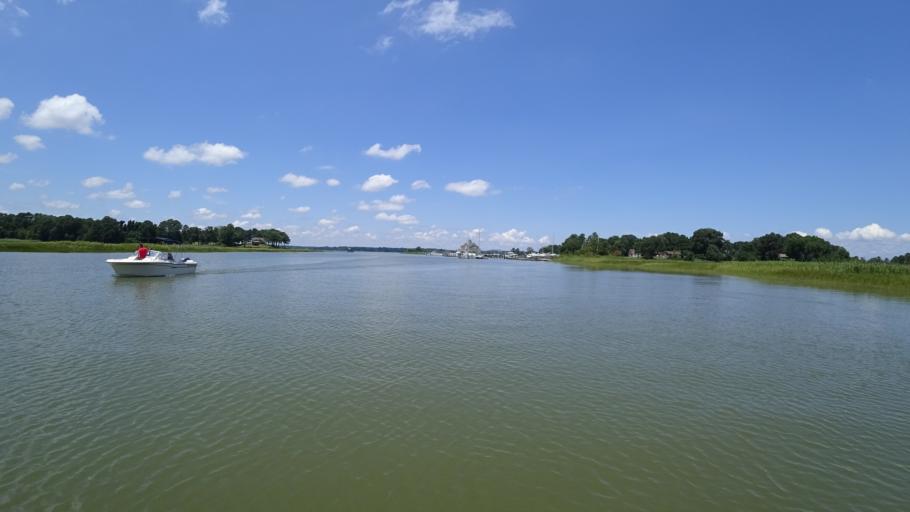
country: US
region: Virginia
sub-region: Isle of Wight County
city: Carrollton
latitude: 36.9962
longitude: -76.5641
